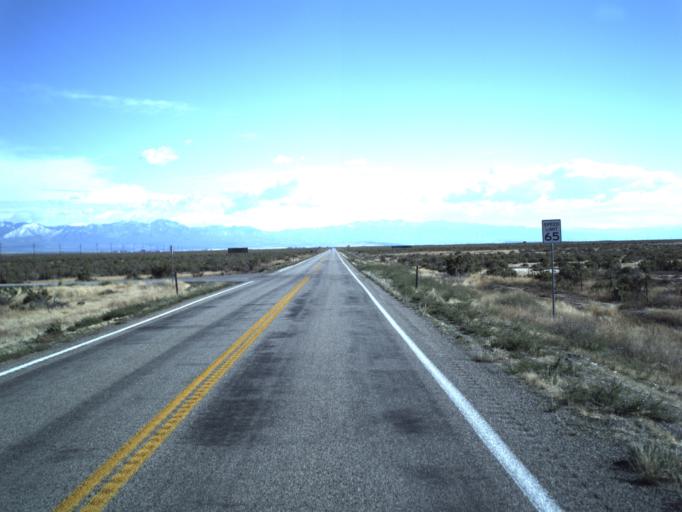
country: US
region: Utah
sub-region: Millard County
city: Delta
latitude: 39.2876
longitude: -112.4643
